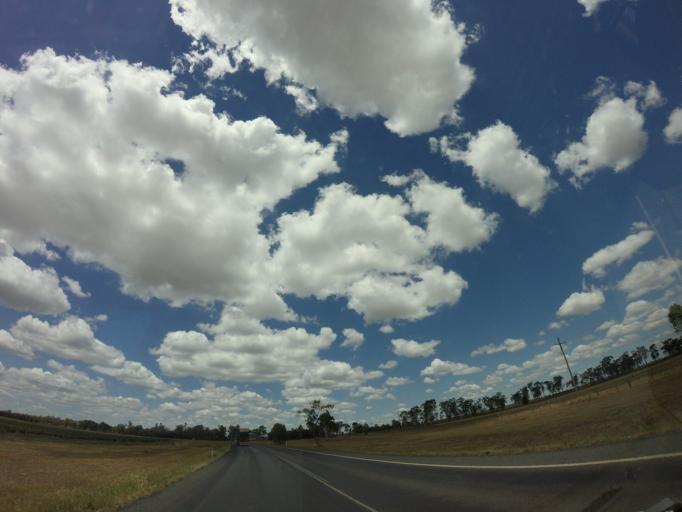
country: AU
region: Queensland
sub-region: Toowoomba
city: Oakey
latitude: -27.8557
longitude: 151.3234
